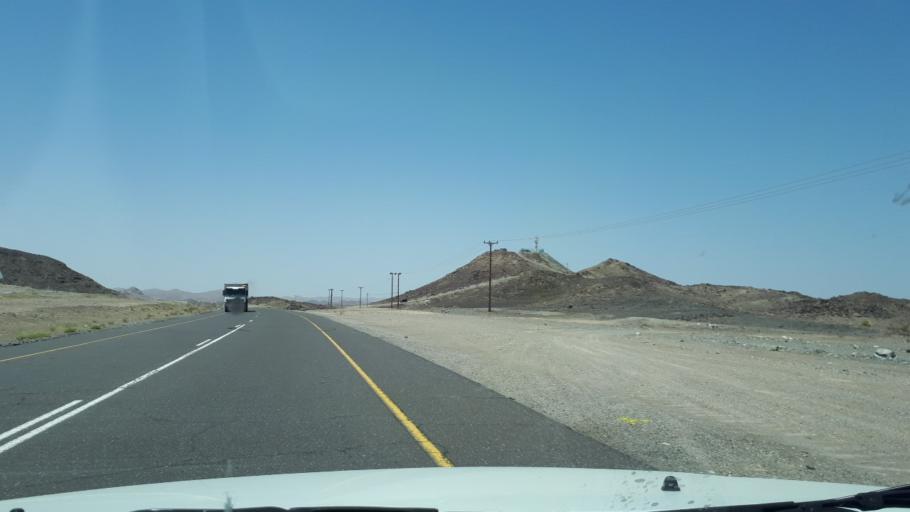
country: OM
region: Ash Sharqiyah
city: Ibra'
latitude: 22.6304
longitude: 58.4591
